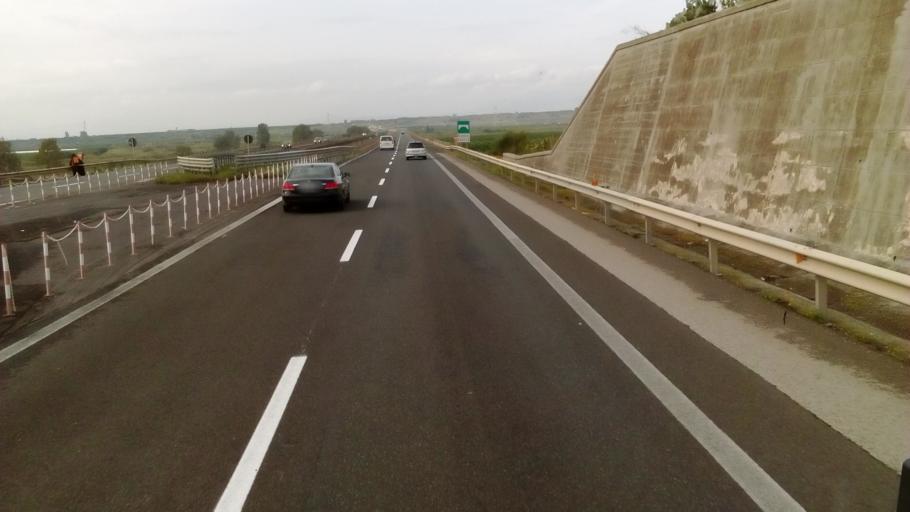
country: IT
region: Sicily
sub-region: Catania
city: Motta Sant'Anastasia
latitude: 37.4685
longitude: 14.9012
